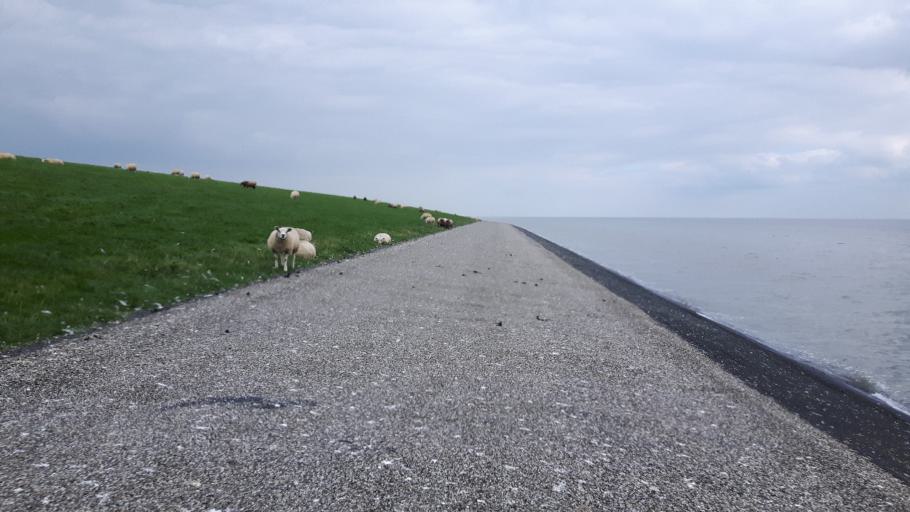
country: NL
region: Friesland
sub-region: Gemeente Ameland
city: Nes
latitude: 53.4437
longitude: 5.8395
